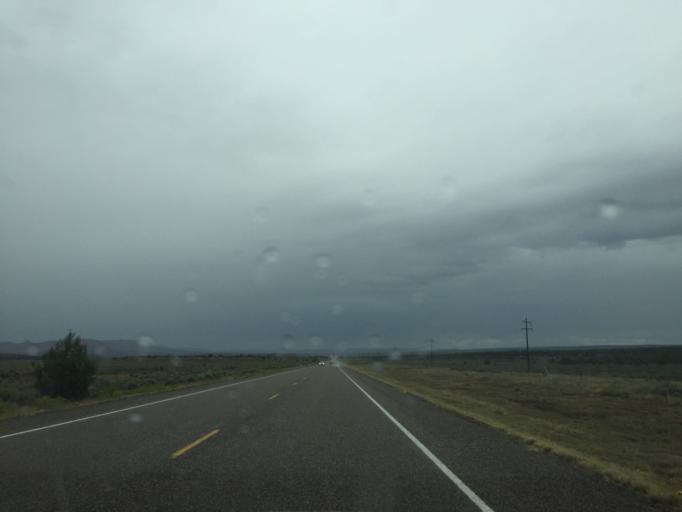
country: US
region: Utah
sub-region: Kane County
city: Kanab
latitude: 37.0908
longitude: -112.1463
